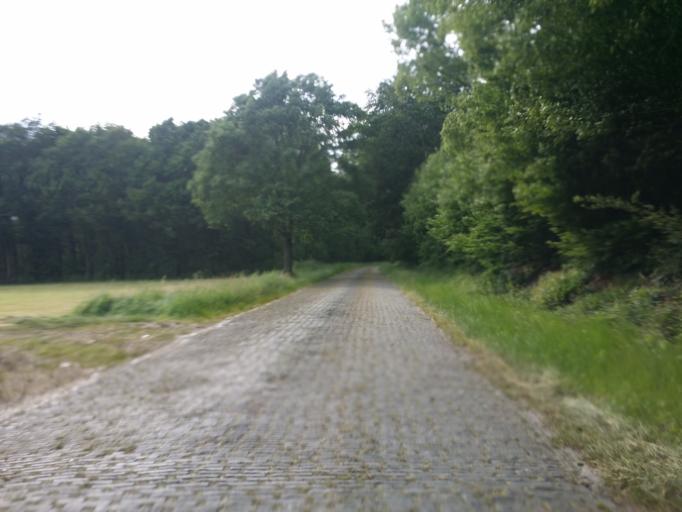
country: DE
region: Lower Saxony
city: Bockhorn
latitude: 53.3748
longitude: 7.9853
